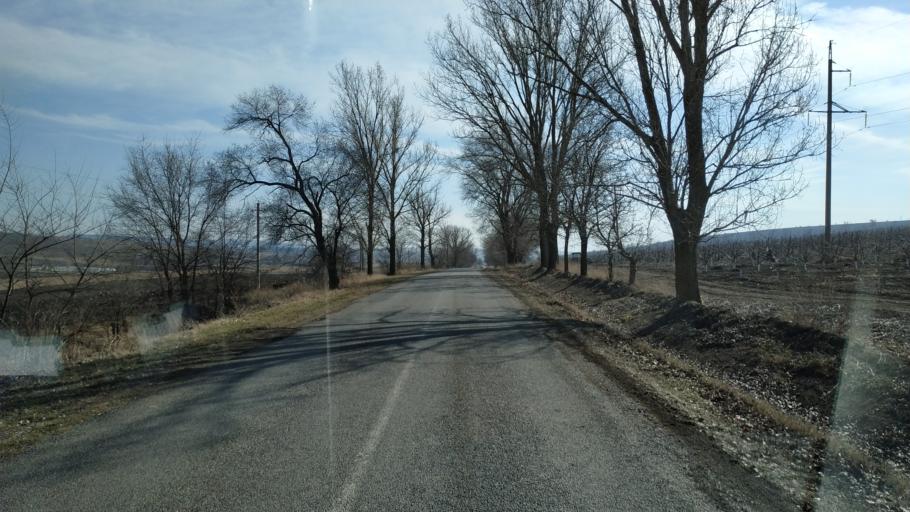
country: MD
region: Nisporeni
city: Nisporeni
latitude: 47.1002
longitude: 28.1291
